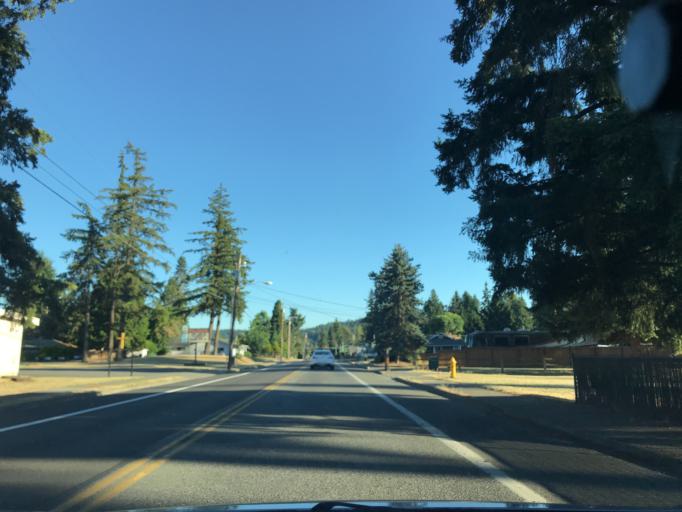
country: US
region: Washington
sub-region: King County
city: Auburn
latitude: 47.2861
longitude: -122.2080
